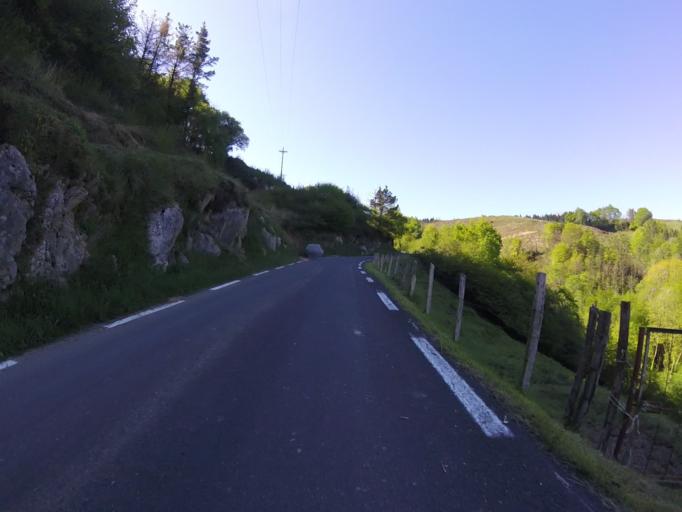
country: ES
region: Basque Country
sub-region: Provincia de Guipuzcoa
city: Aizarnazabal
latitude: 43.2211
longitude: -2.2125
